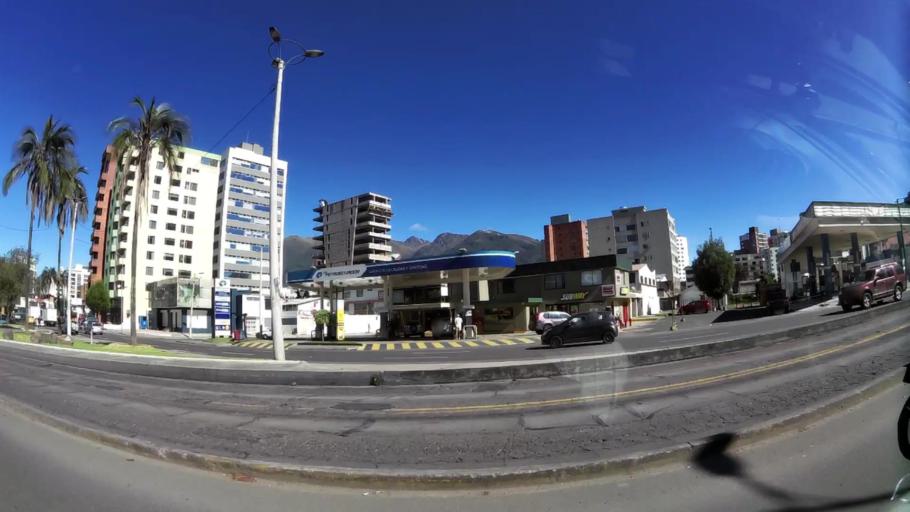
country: EC
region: Pichincha
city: Quito
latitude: -0.1897
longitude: -78.4805
